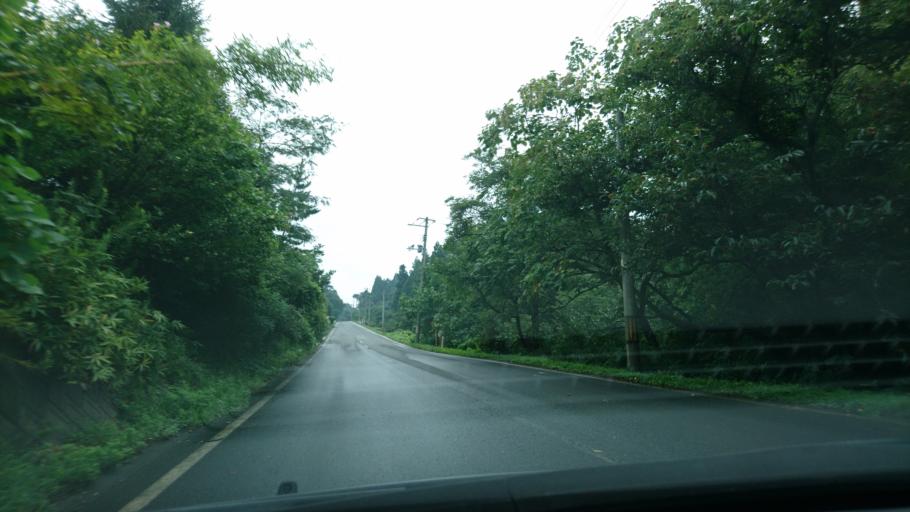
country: JP
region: Iwate
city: Ichinoseki
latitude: 38.9368
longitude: 141.1863
